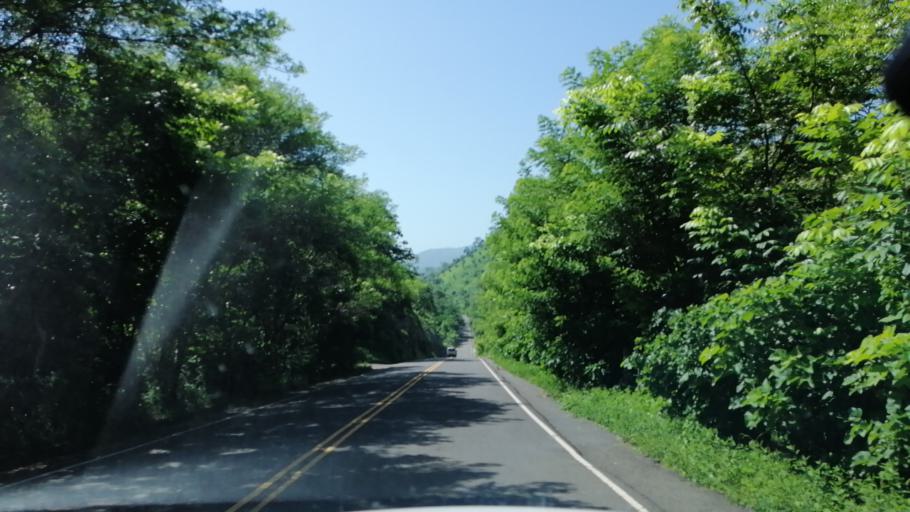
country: HN
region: Lempira
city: La Virtud
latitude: 13.9580
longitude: -88.7537
